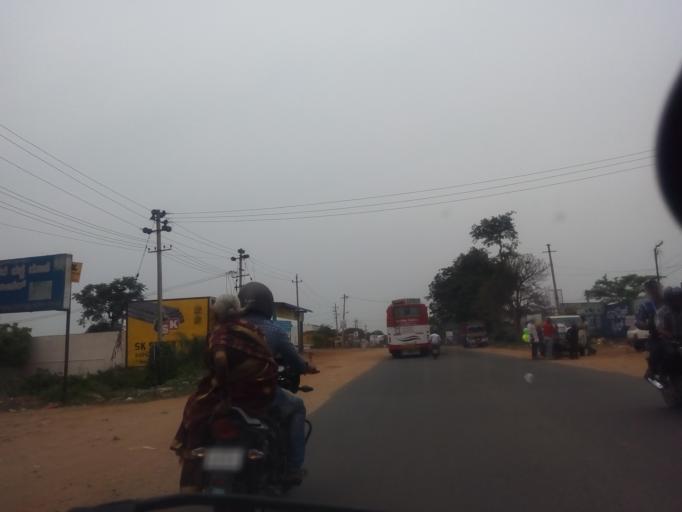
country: IN
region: Karnataka
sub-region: Bangalore Rural
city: Nelamangala
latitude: 12.9918
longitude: 77.4628
